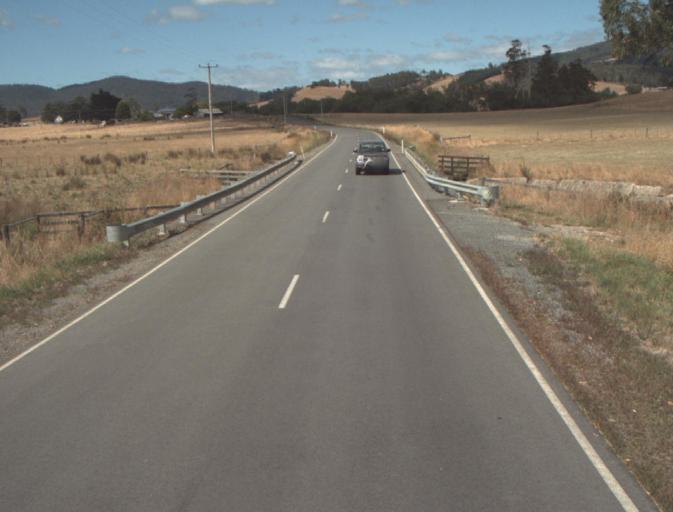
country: AU
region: Tasmania
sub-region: Launceston
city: Mayfield
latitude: -41.2202
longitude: 147.1375
